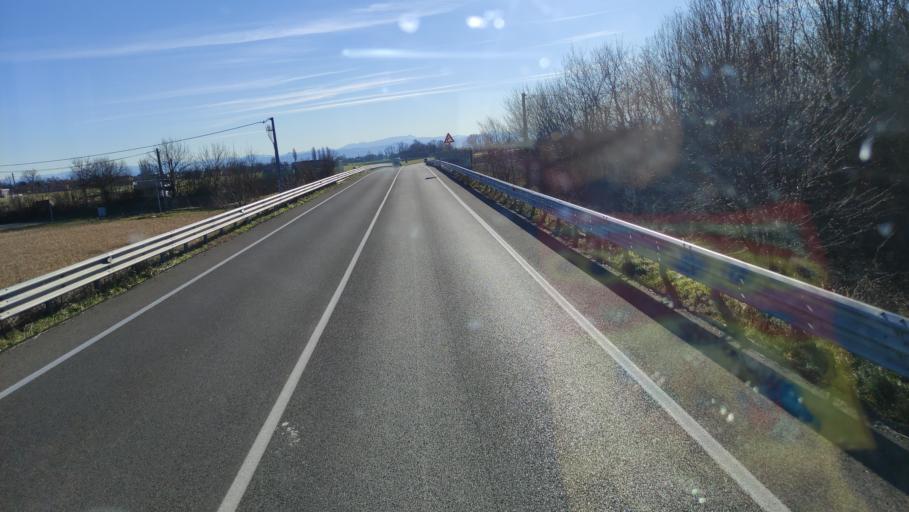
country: IT
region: Emilia-Romagna
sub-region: Provincia di Reggio Emilia
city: Bagnolo in Piano
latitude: 44.7925
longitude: 10.6777
